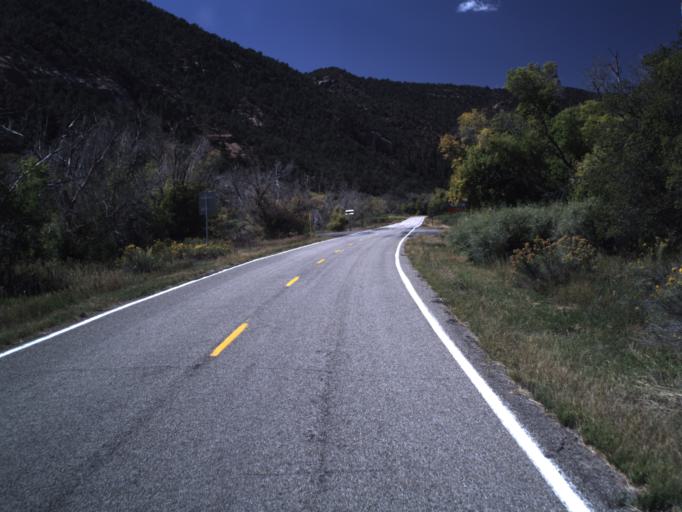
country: US
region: Utah
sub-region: San Juan County
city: Monticello
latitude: 38.3281
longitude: -109.0585
